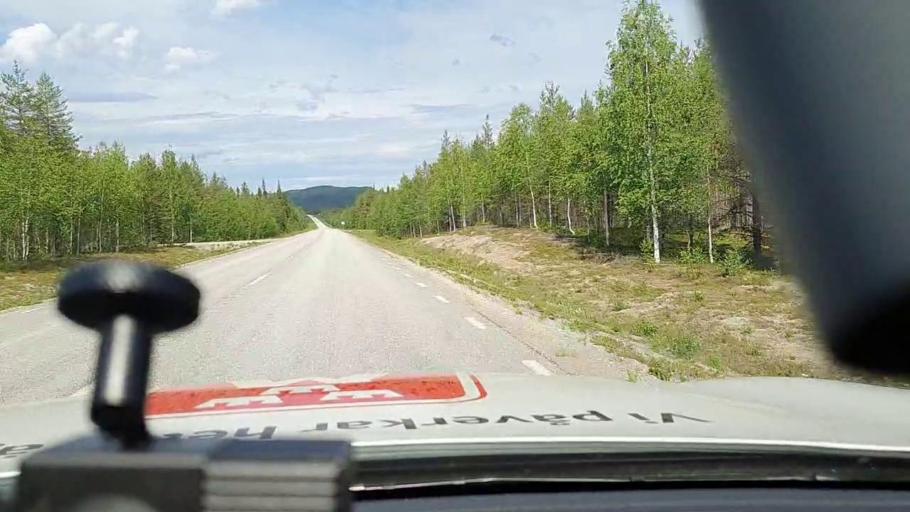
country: SE
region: Norrbotten
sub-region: Jokkmokks Kommun
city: Jokkmokk
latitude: 66.5441
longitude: 20.1380
